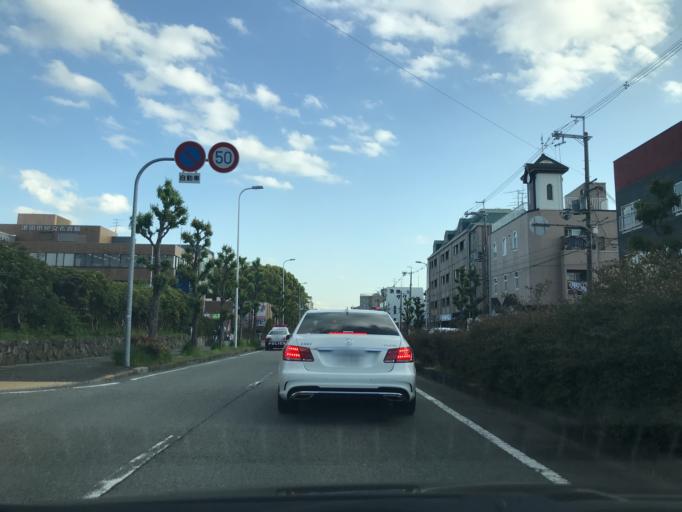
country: JP
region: Osaka
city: Ikeda
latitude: 34.8100
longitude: 135.4402
